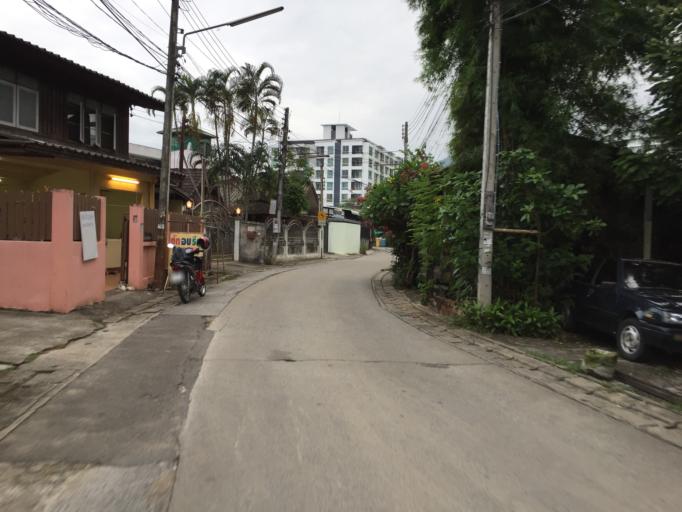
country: TH
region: Chiang Mai
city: Chiang Mai
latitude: 18.8022
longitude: 98.9626
